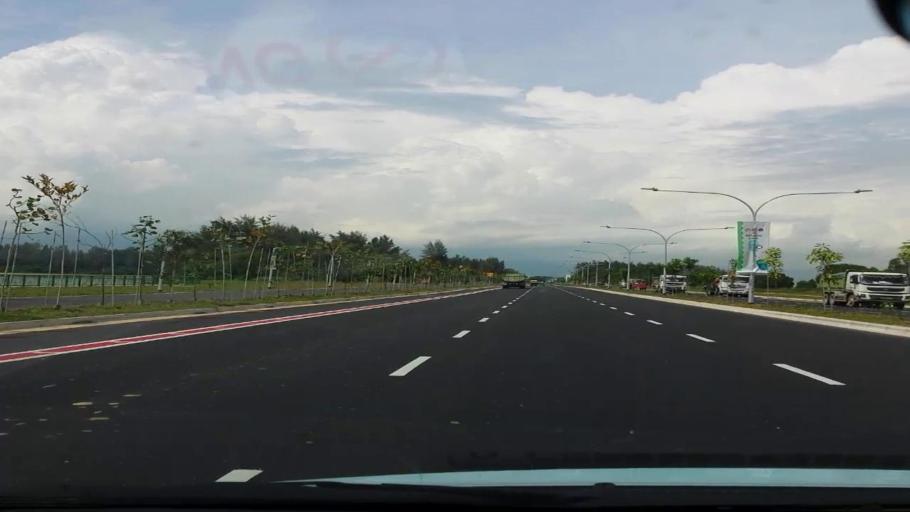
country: SG
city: Singapore
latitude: 1.3336
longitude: 104.0222
